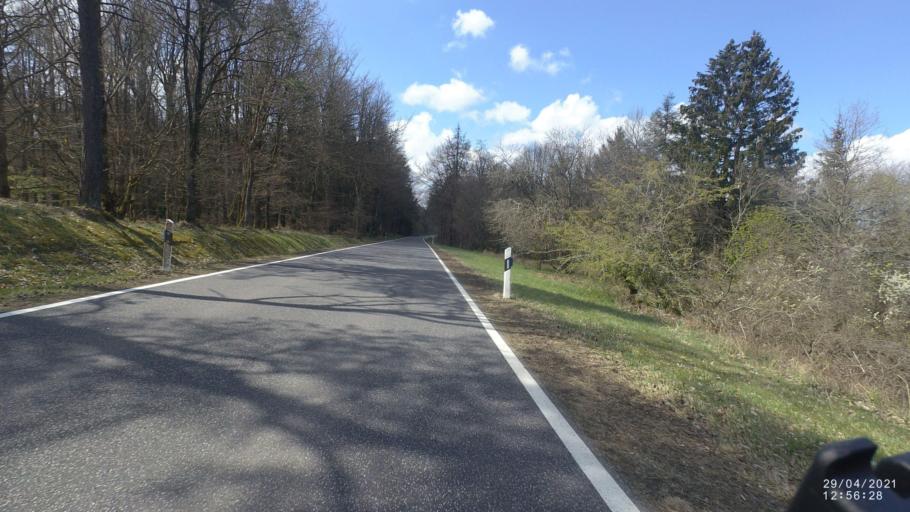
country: DE
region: Rheinland-Pfalz
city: Langscheid
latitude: 50.3686
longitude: 7.1175
